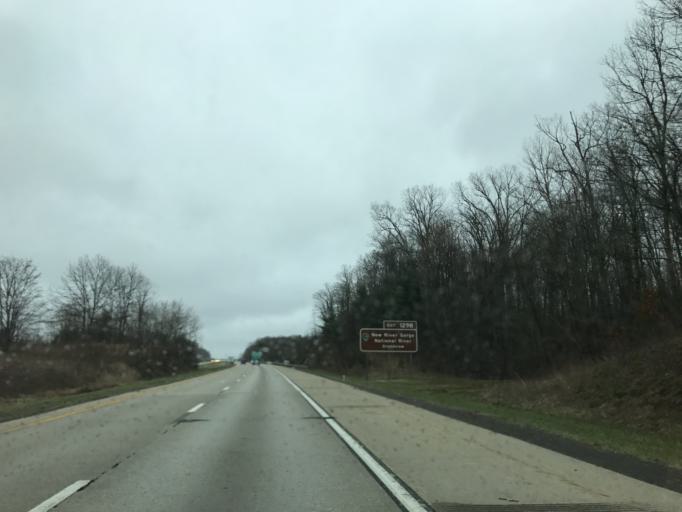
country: US
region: West Virginia
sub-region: Raleigh County
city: Daniels
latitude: 37.7738
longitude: -81.0860
